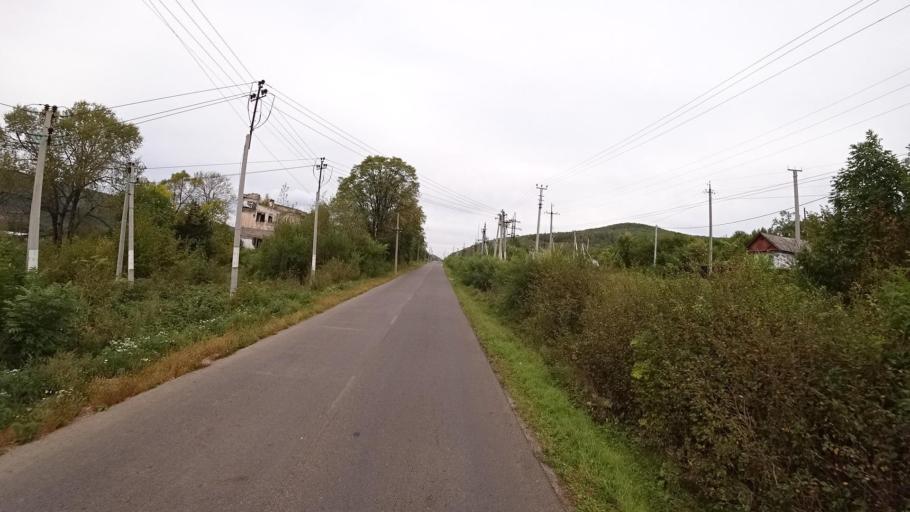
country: RU
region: Jewish Autonomous Oblast
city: Khingansk
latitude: 49.0351
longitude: 131.0588
